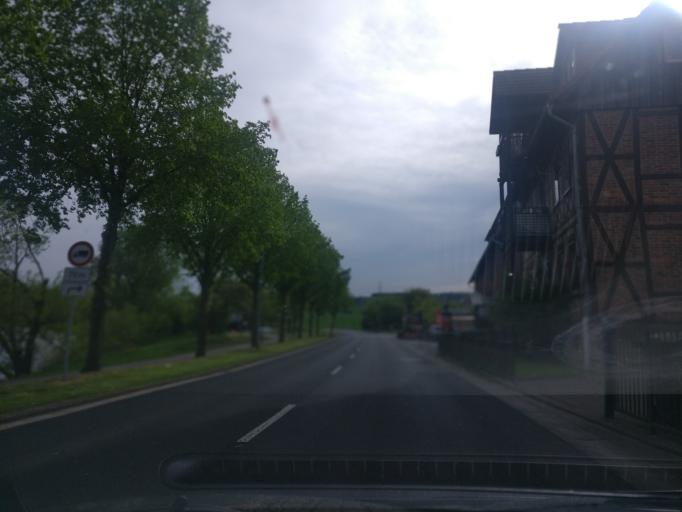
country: DE
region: Hesse
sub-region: Regierungsbezirk Kassel
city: Fuldatal
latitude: 51.4023
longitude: 9.5773
